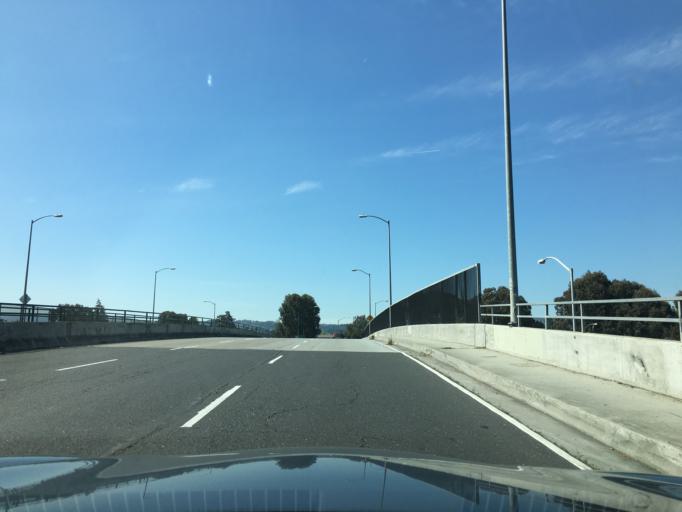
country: US
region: California
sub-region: San Mateo County
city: San Mateo
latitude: 37.5714
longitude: -122.3136
